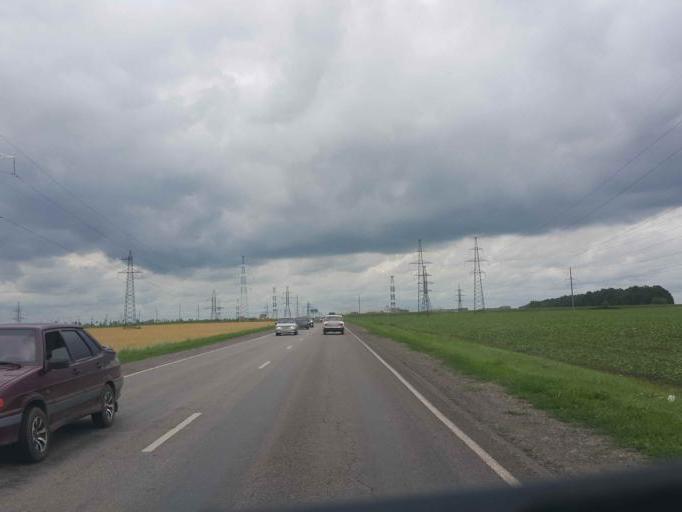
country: RU
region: Tambov
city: Komsomolets
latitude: 52.7784
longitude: 41.3460
